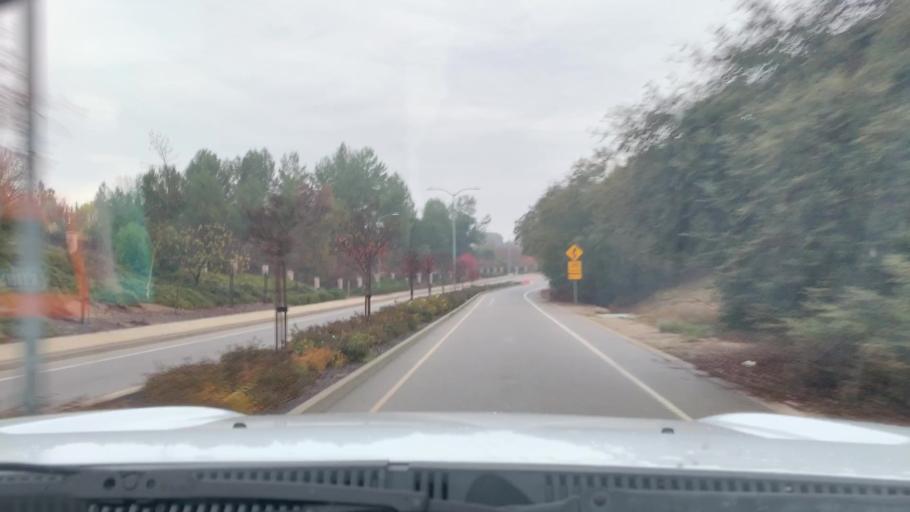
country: US
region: California
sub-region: San Luis Obispo County
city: Paso Robles
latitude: 35.6349
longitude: -120.6710
